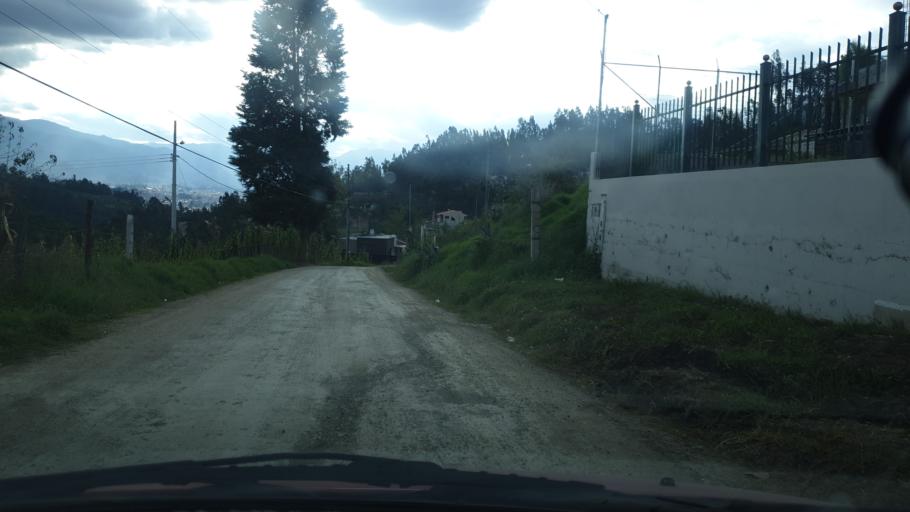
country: EC
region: Azuay
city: Cuenca
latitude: -2.9200
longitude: -78.9752
